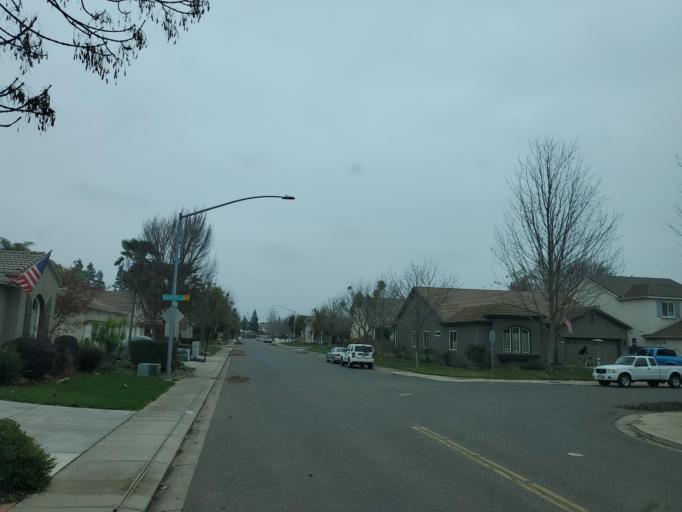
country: US
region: California
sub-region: Stanislaus County
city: Salida
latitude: 37.7018
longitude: -121.0380
